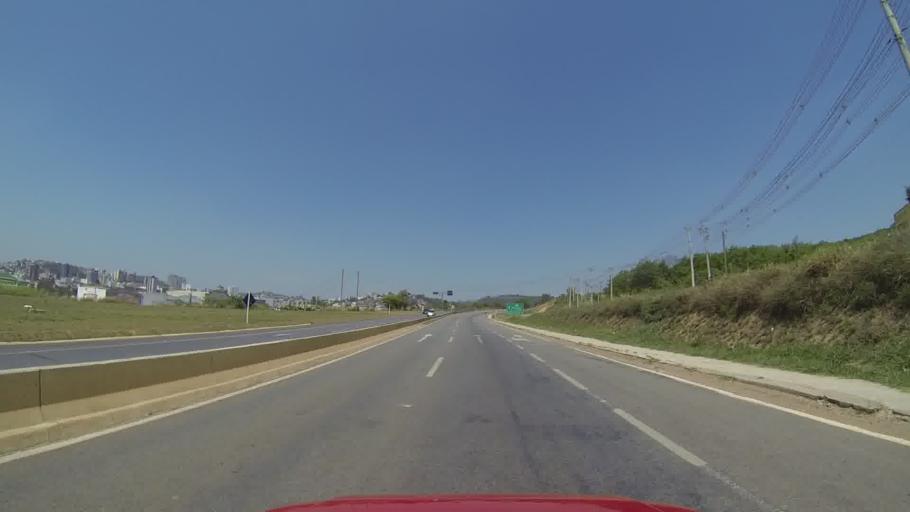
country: BR
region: Minas Gerais
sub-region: Itauna
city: Itauna
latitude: -20.0629
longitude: -44.5745
